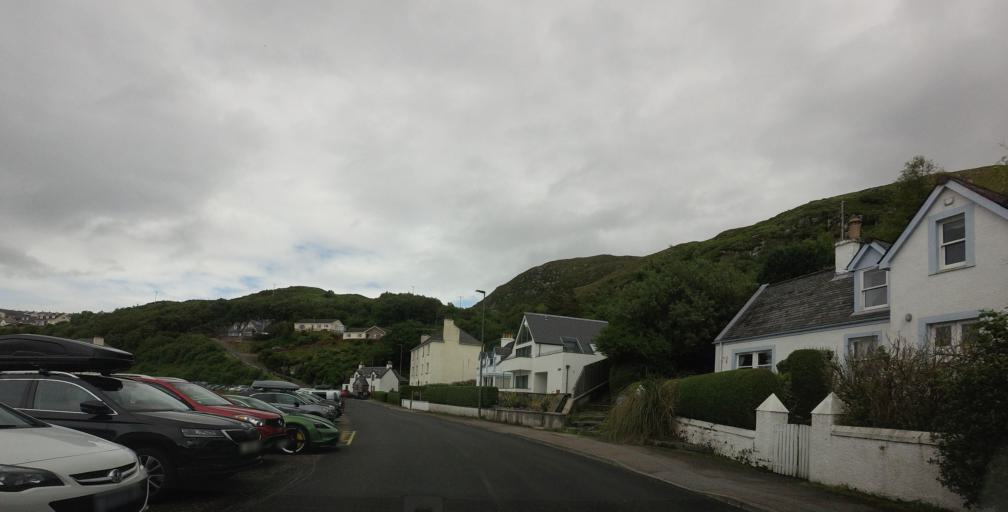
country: GB
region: Scotland
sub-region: Highland
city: Portree
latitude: 57.0042
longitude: -5.8239
